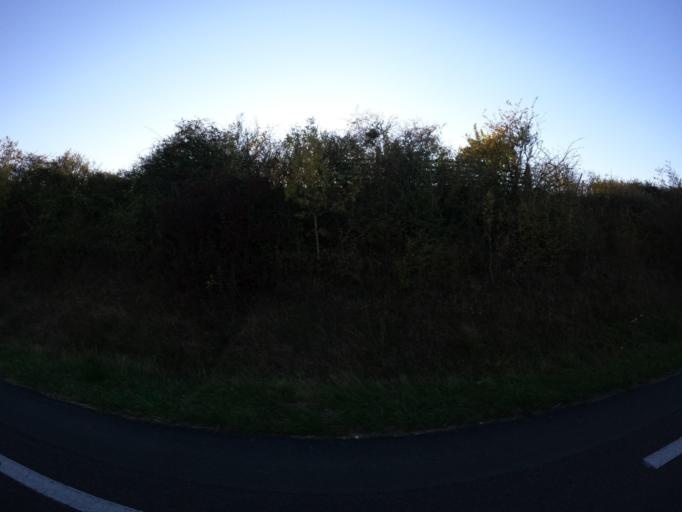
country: FR
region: Pays de la Loire
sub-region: Departement de la Vendee
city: Sainte-Hermine
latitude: 46.5590
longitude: -1.0460
